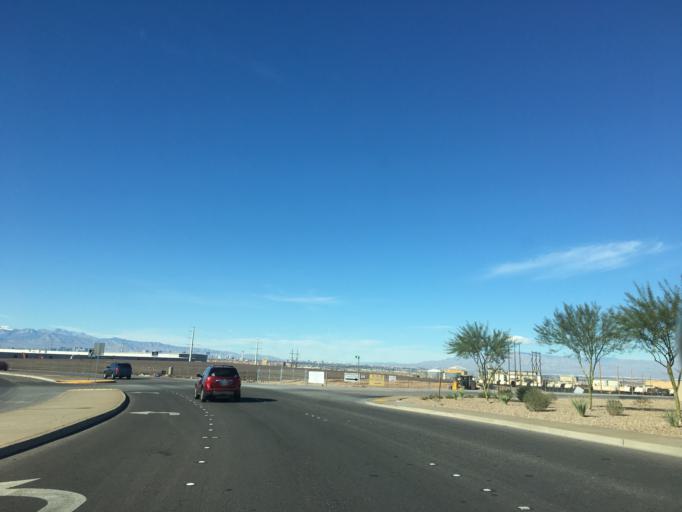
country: US
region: Nevada
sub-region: Clark County
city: Henderson
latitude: 36.0354
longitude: -115.0082
